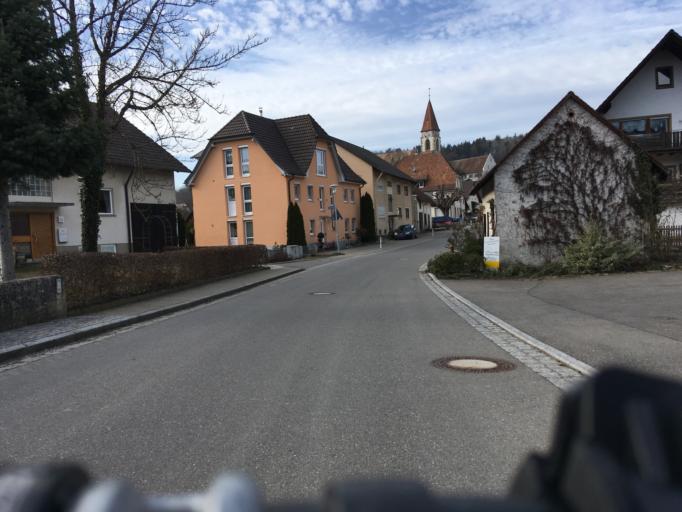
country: DE
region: Baden-Wuerttemberg
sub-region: Freiburg Region
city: Tengen
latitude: 47.7918
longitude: 8.6869
